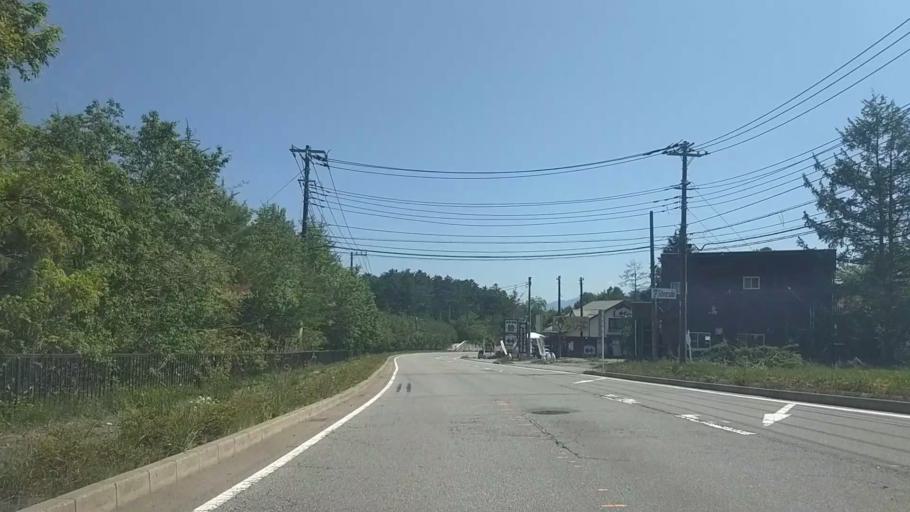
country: JP
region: Yamanashi
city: Nirasaki
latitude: 35.8926
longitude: 138.4403
